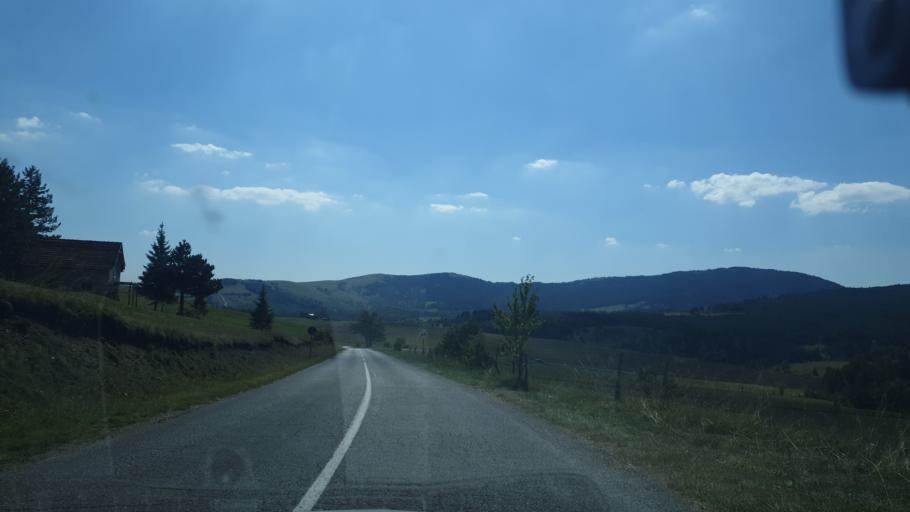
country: RS
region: Central Serbia
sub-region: Zlatiborski Okrug
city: Kosjeric
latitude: 44.0761
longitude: 20.0211
